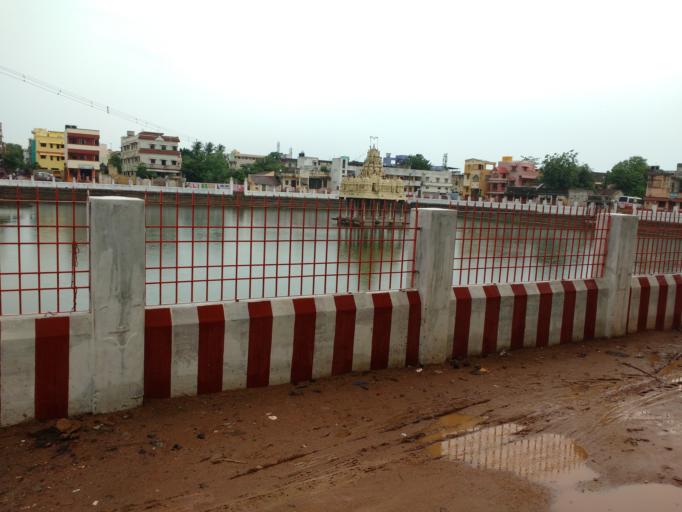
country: IN
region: Tamil Nadu
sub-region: Kancheepuram
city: Sriperumbudur
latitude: 12.9677
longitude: 79.9471
